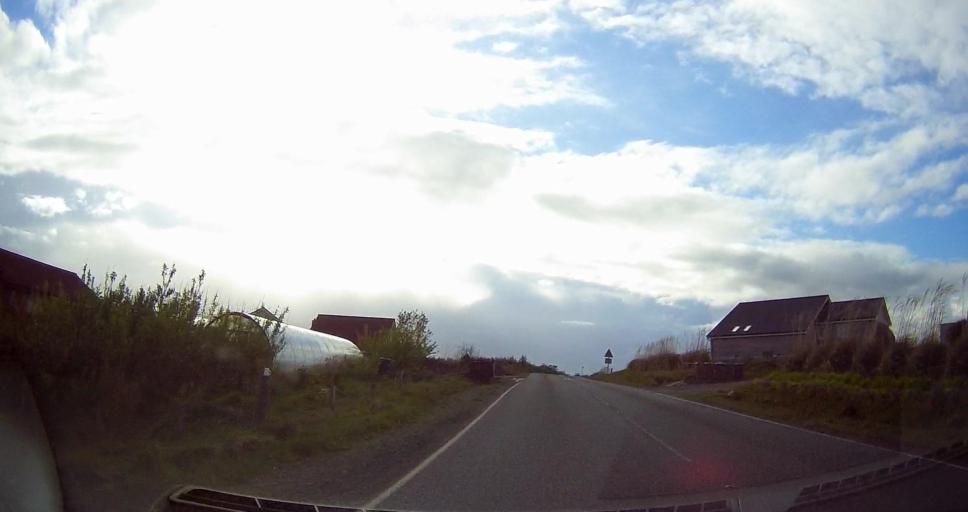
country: GB
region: Scotland
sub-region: Shetland Islands
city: Lerwick
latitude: 60.3860
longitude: -1.3433
